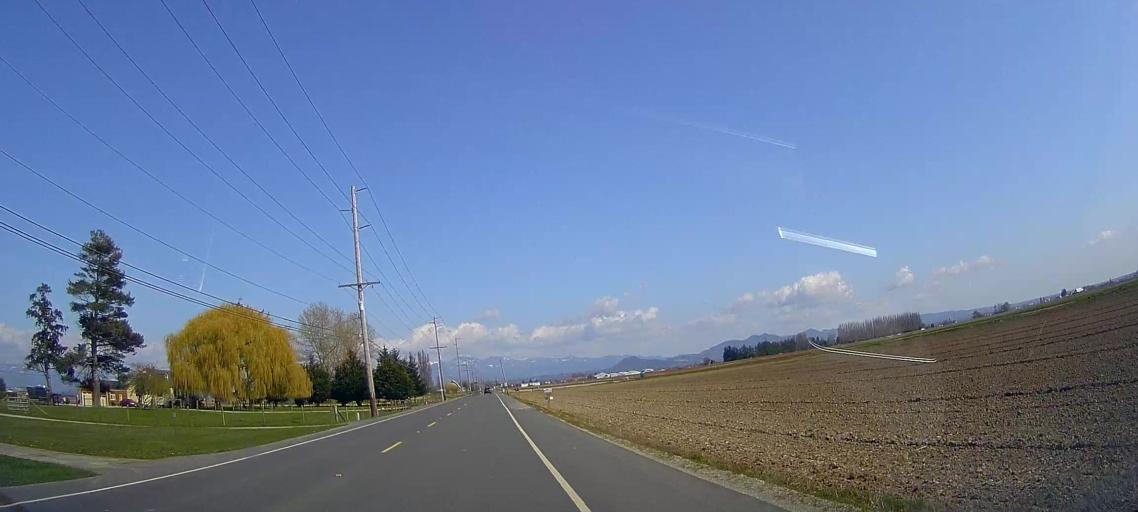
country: US
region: Washington
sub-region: Skagit County
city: Mount Vernon
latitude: 48.4211
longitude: -122.4599
